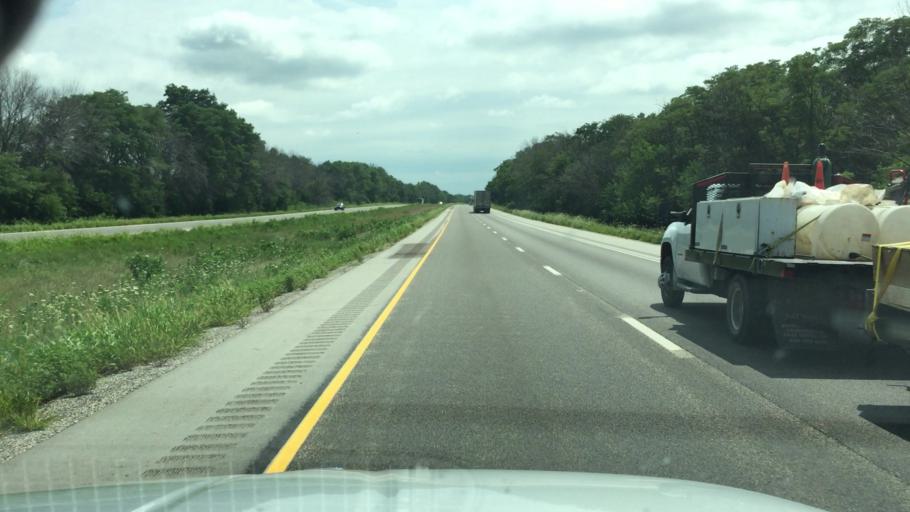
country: US
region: Illinois
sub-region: Peoria County
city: Elmwood
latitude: 40.8680
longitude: -90.0348
